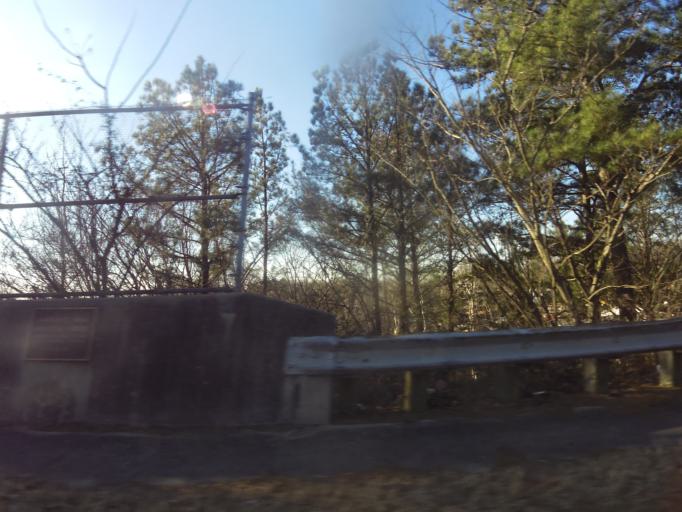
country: US
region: Virginia
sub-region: City of Hopewell
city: Hopewell
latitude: 37.2990
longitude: -77.2913
